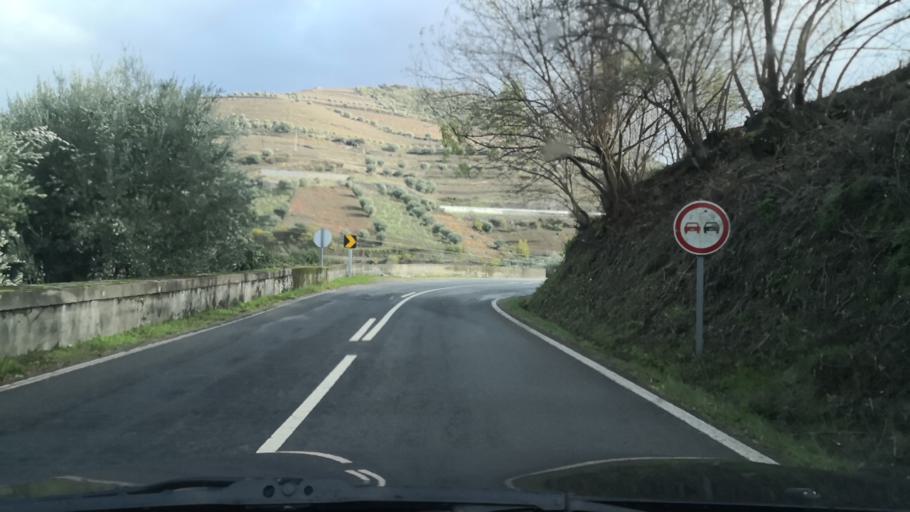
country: PT
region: Vila Real
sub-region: Peso da Regua
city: Peso da Regua
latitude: 41.1483
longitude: -7.7802
